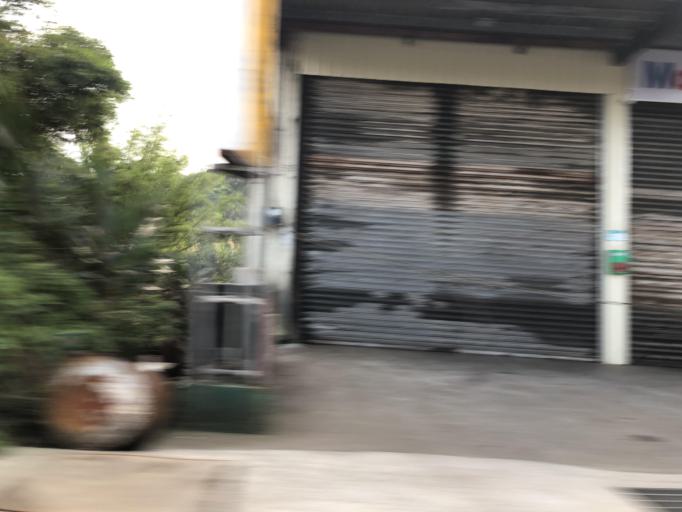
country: TW
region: Taiwan
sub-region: Keelung
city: Keelung
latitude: 25.2169
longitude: 121.6421
